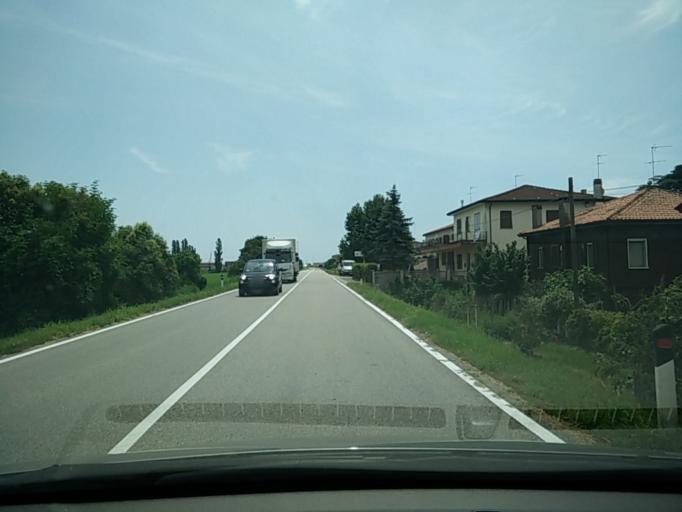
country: IT
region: Veneto
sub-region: Provincia di Venezia
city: Meolo
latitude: 45.5613
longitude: 12.4439
